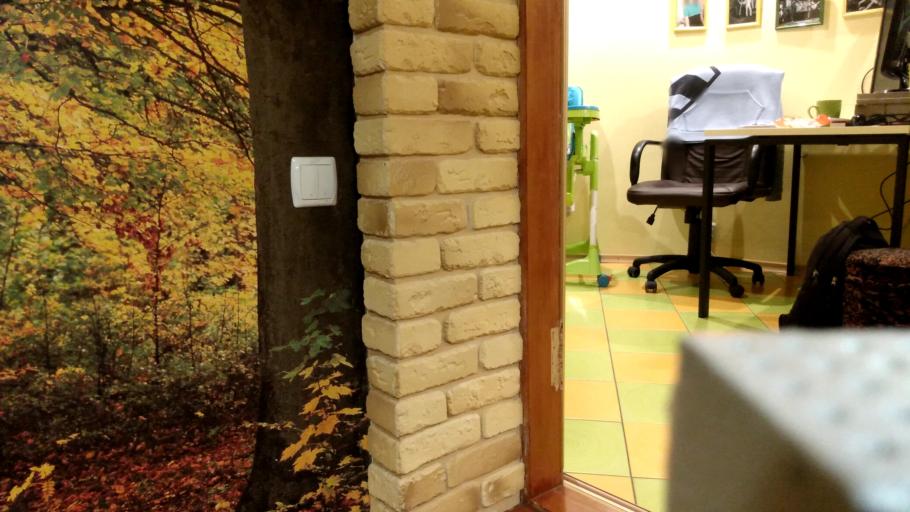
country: RU
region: Republic of Karelia
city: Pudozh
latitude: 61.8175
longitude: 37.6654
